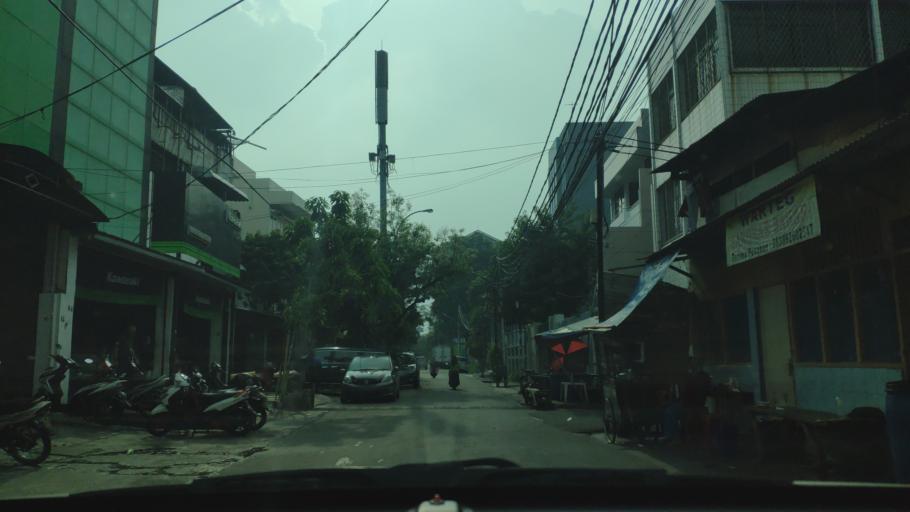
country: ID
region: Jakarta Raya
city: Jakarta
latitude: -6.1569
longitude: 106.8203
